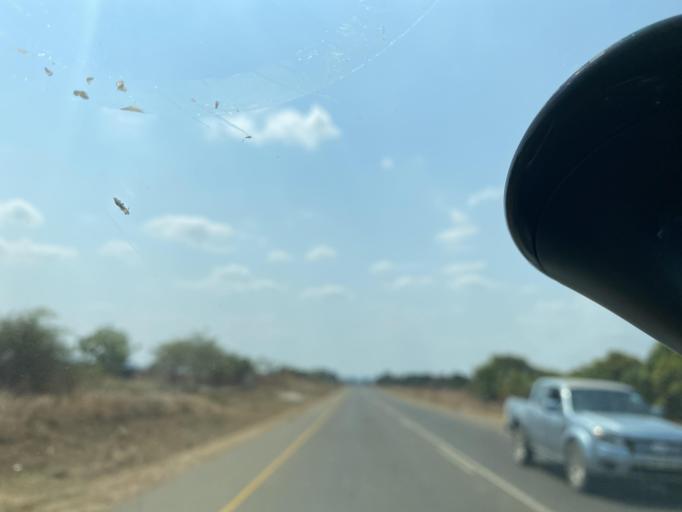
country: ZM
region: Lusaka
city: Chongwe
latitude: -15.5921
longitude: 28.7150
